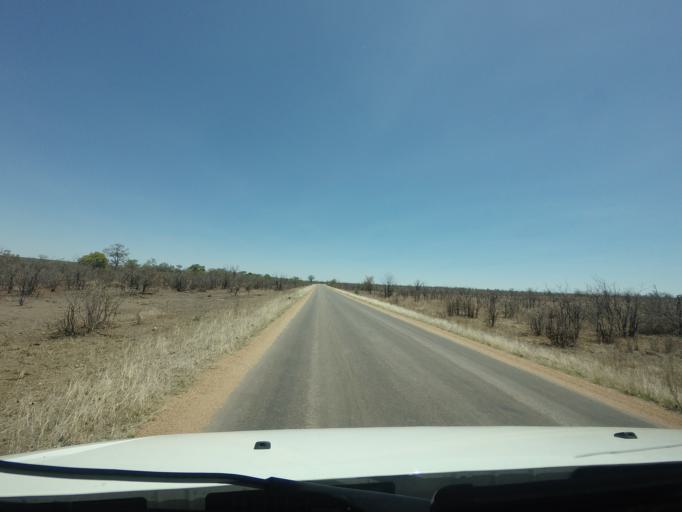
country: ZA
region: Limpopo
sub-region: Mopani District Municipality
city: Phalaborwa
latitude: -23.5915
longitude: 31.4531
